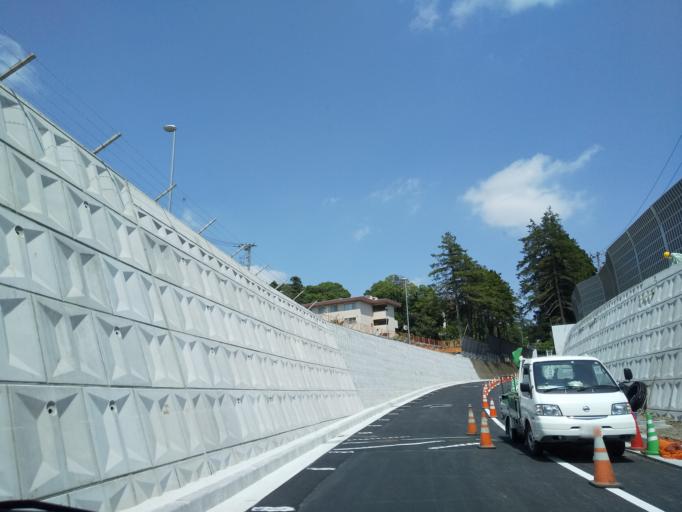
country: JP
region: Kanagawa
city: Zama
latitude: 35.4990
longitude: 139.3997
